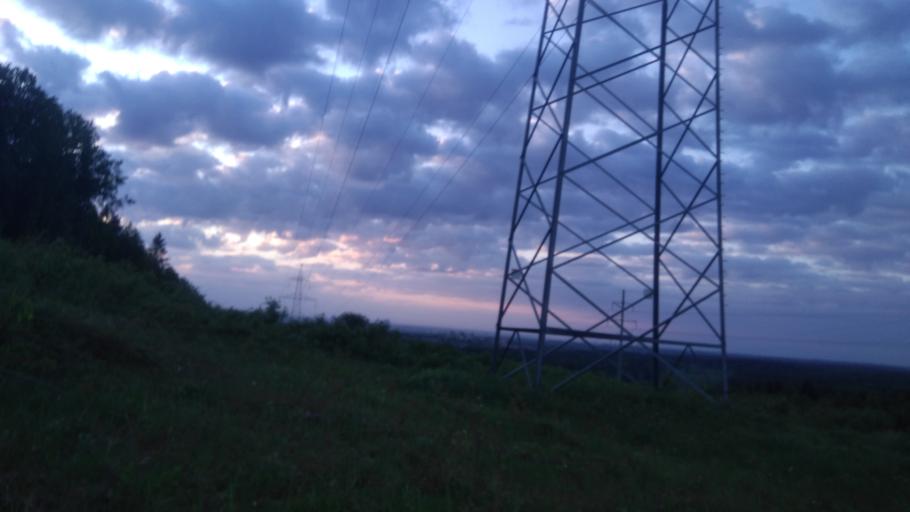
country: RU
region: Perm
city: Ferma
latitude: 57.9689
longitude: 56.3459
